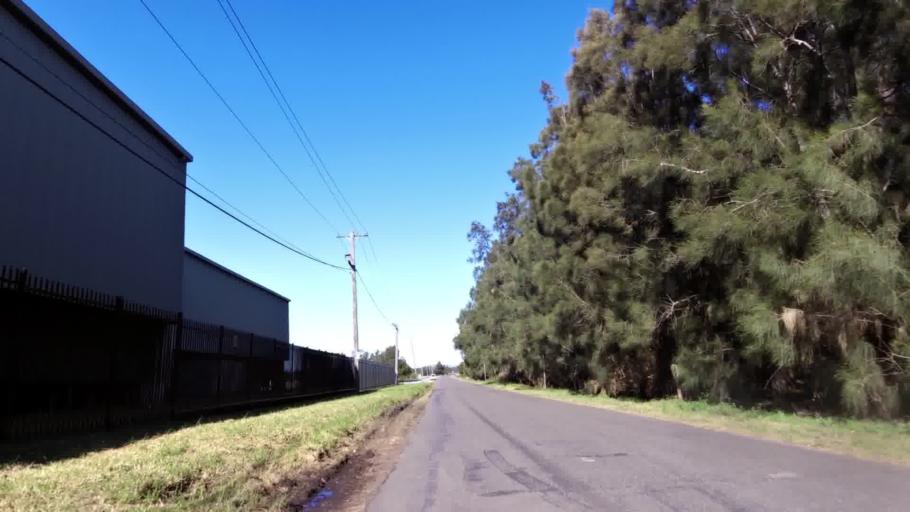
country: AU
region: New South Wales
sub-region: Wollongong
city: Berkeley
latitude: -34.4783
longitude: 150.8339
